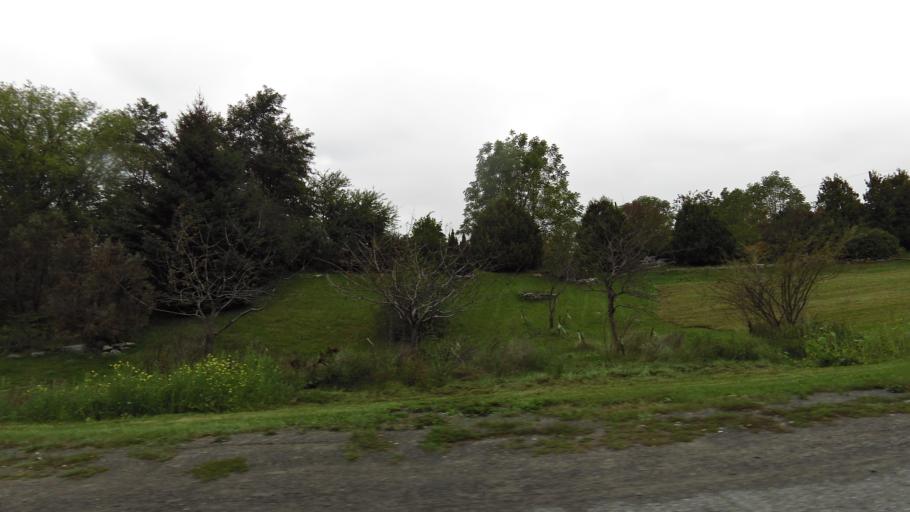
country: CA
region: Ontario
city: Kingston
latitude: 44.2393
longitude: -76.4598
